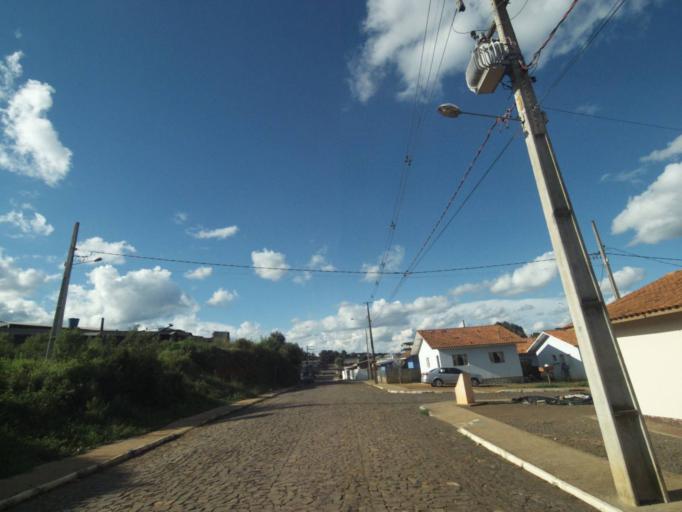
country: BR
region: Parana
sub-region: Uniao Da Vitoria
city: Uniao da Vitoria
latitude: -26.1621
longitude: -51.5334
